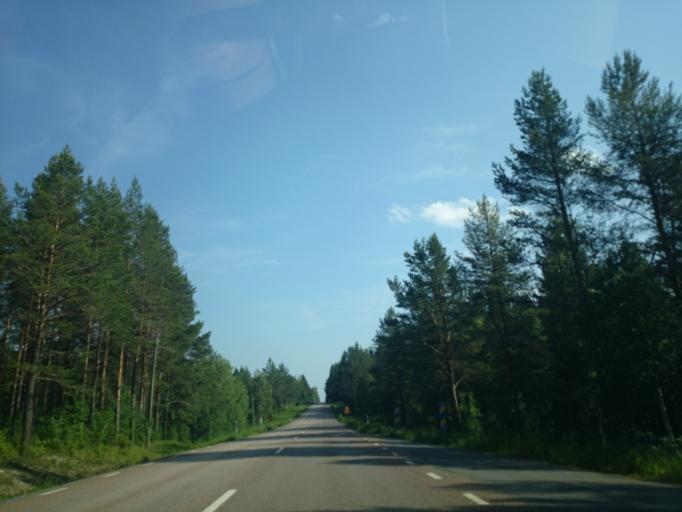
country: SE
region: Jaemtland
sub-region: OEstersunds Kommun
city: Brunflo
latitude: 63.0614
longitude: 14.8513
